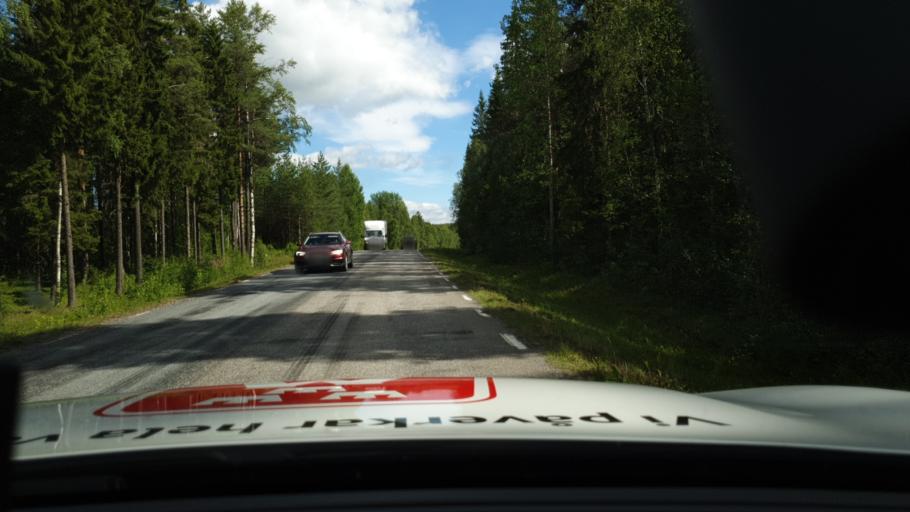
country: SE
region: Norrbotten
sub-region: Lulea Kommun
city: Ranea
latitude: 65.7756
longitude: 22.2073
